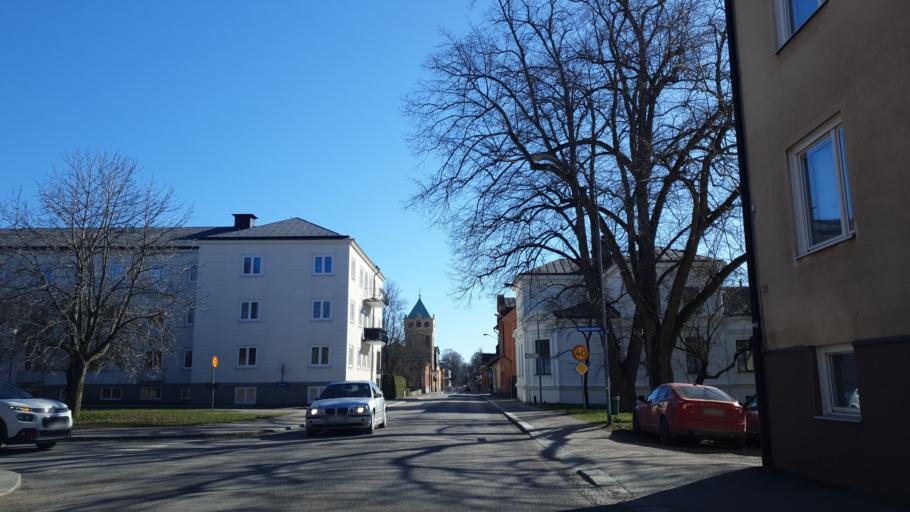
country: SE
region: Vaestmanland
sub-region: Kopings Kommun
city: Koping
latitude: 59.5118
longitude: 15.9989
